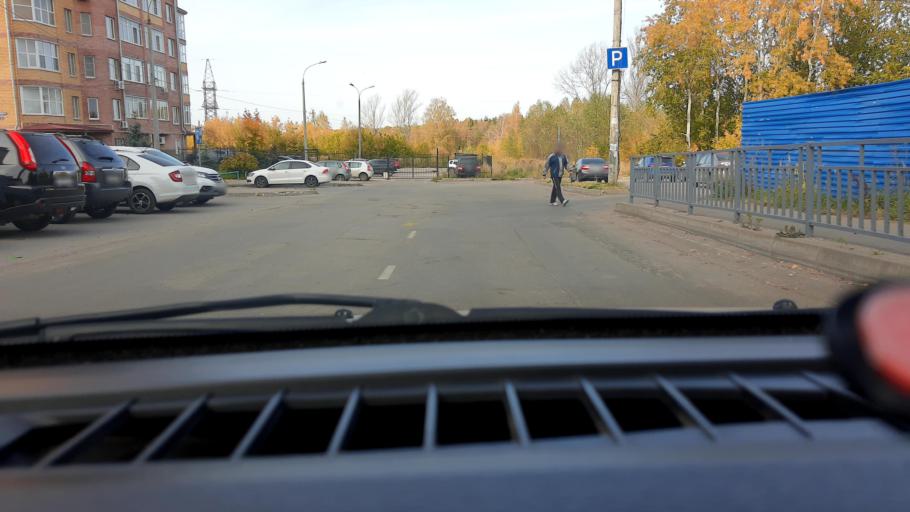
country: RU
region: Nizjnij Novgorod
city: Kstovo
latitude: 56.1530
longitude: 44.1850
